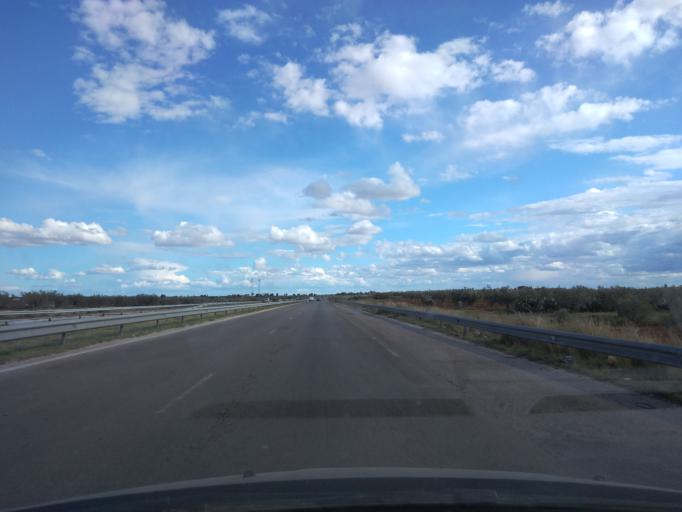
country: TN
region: Al Munastir
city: Manzil Kamil
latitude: 35.6342
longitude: 10.5848
